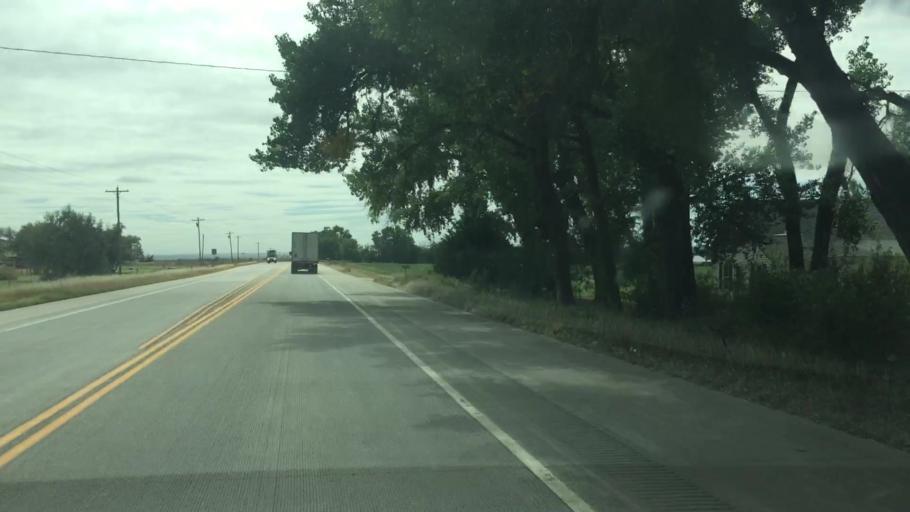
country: US
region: Colorado
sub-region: Prowers County
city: Lamar
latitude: 38.2047
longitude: -102.7242
